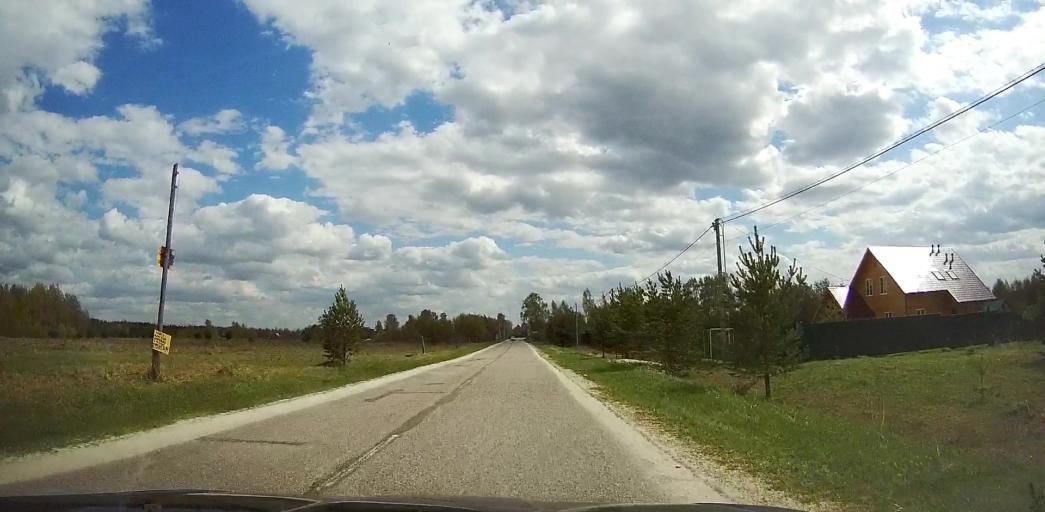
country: RU
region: Moskovskaya
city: Davydovo
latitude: 55.6415
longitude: 38.7755
